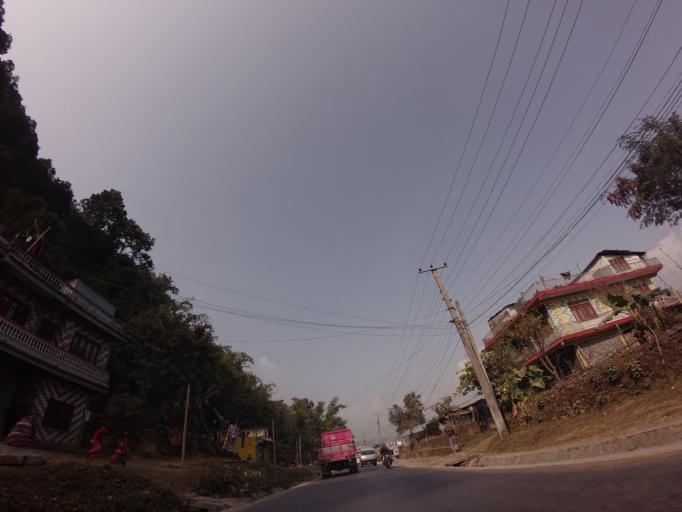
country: NP
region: Western Region
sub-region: Gandaki Zone
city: Pokhara
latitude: 28.2474
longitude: 83.9770
